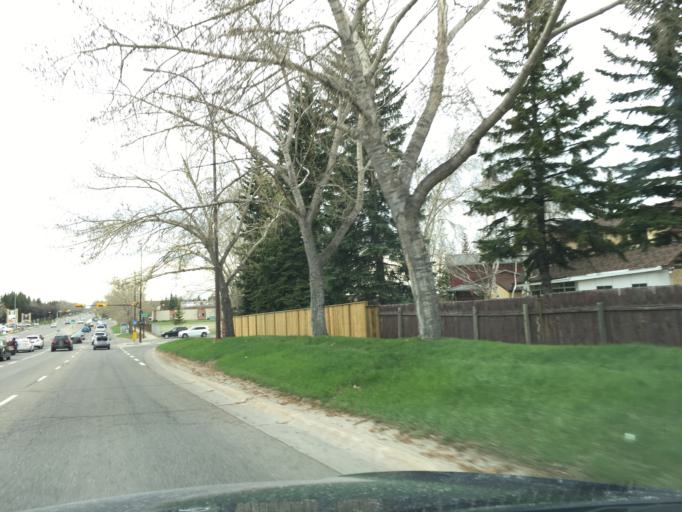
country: CA
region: Alberta
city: Calgary
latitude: 50.9615
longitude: -114.1020
